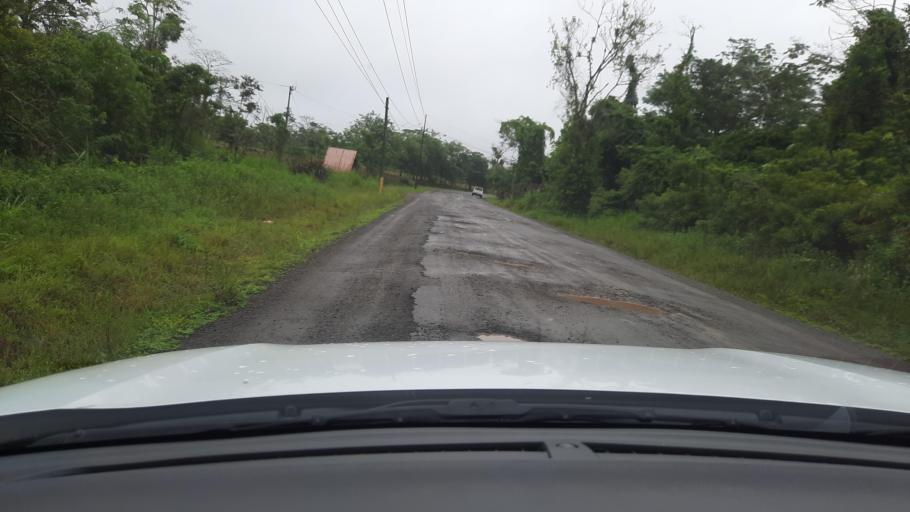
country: CR
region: Alajuela
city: San Jose
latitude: 11.0175
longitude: -85.3531
